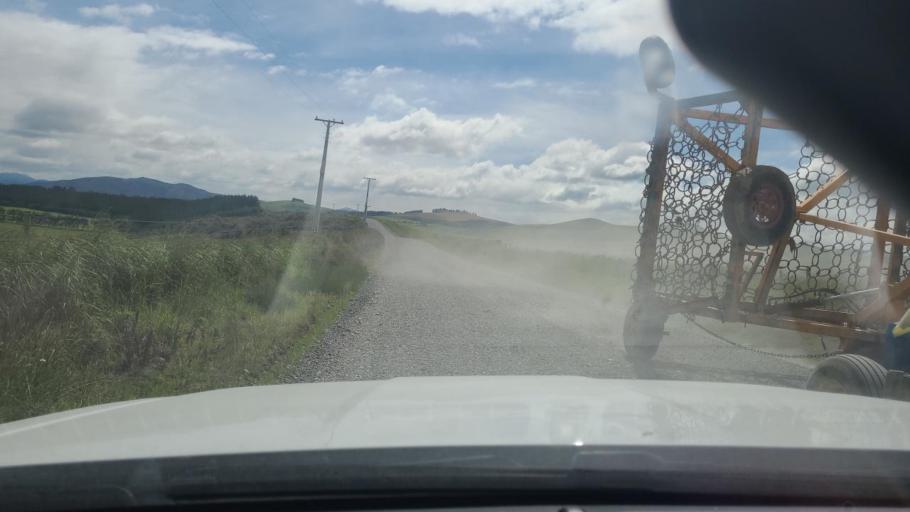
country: NZ
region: Southland
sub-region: Southland District
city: Te Anau
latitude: -45.5259
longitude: 167.8680
